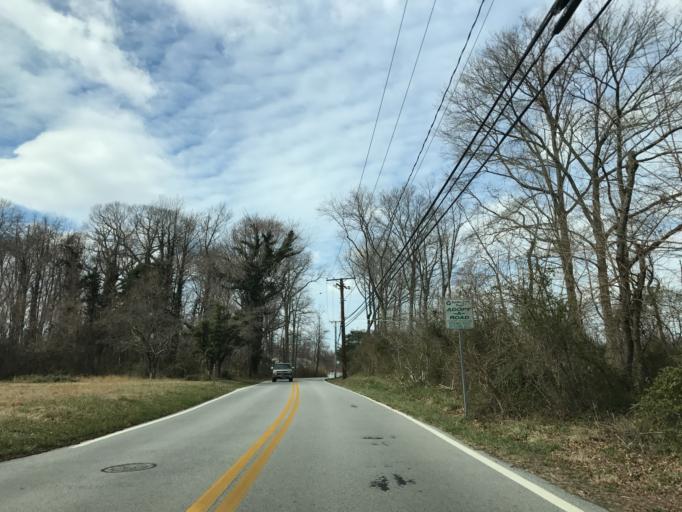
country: US
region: Maryland
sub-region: Baltimore County
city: Middle River
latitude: 39.2948
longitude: -76.4146
